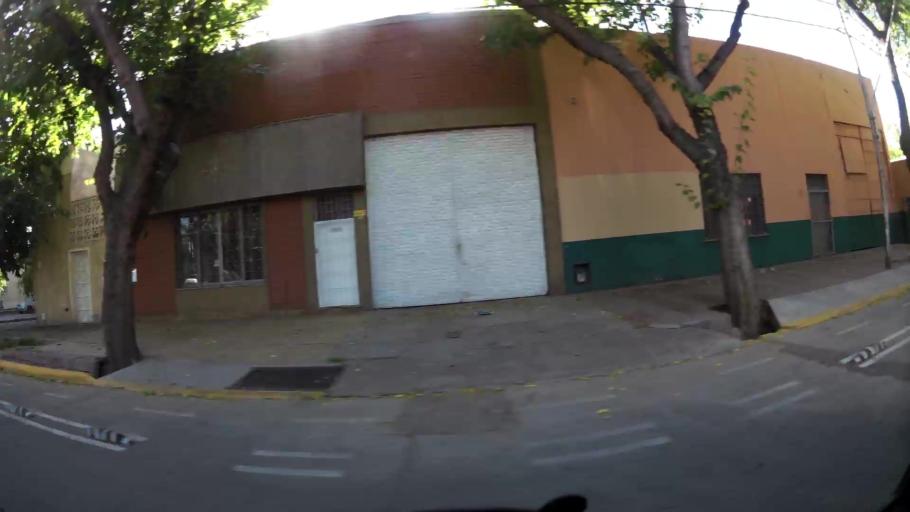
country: AR
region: Mendoza
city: Las Heras
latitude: -32.8682
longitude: -68.8256
